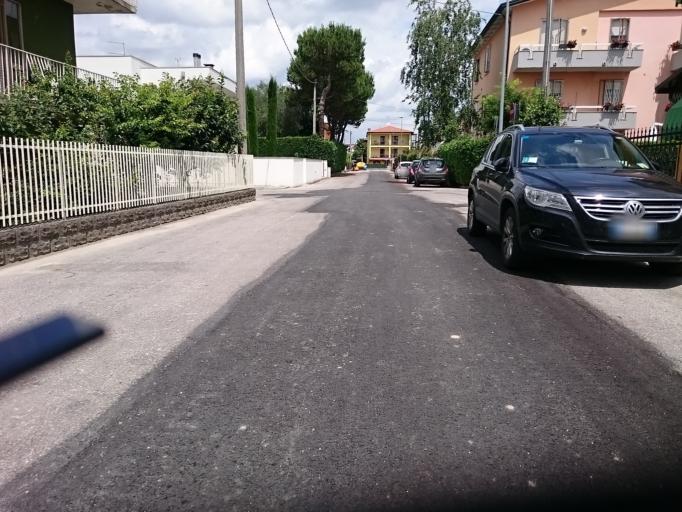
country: IT
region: Veneto
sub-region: Provincia di Padova
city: Caselle
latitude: 45.4101
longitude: 11.8240
